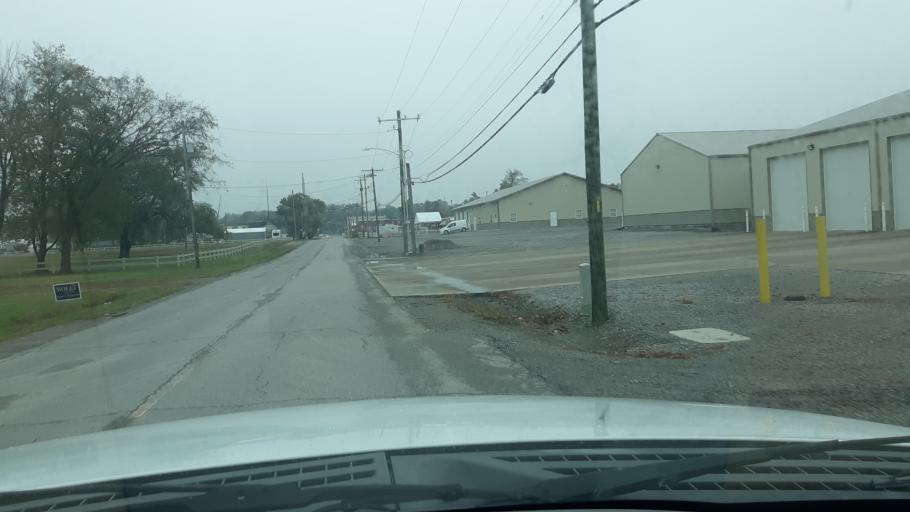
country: US
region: Illinois
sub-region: Saline County
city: Eldorado
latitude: 37.8099
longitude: -88.4354
